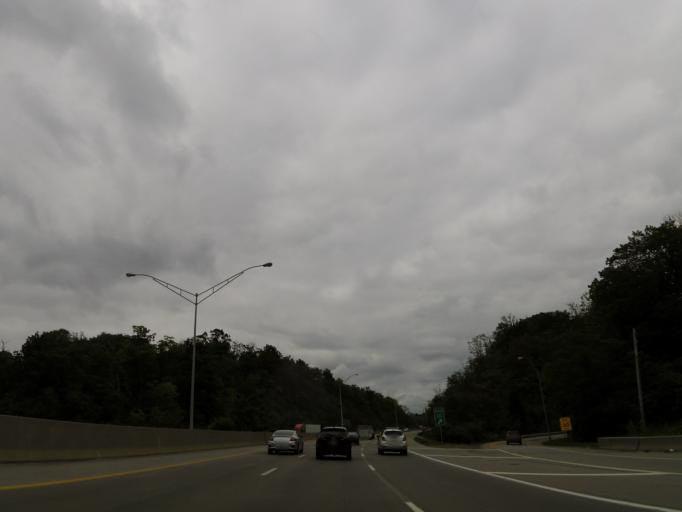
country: US
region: Ohio
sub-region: Hamilton County
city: Silverton
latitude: 39.1837
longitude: -84.3954
